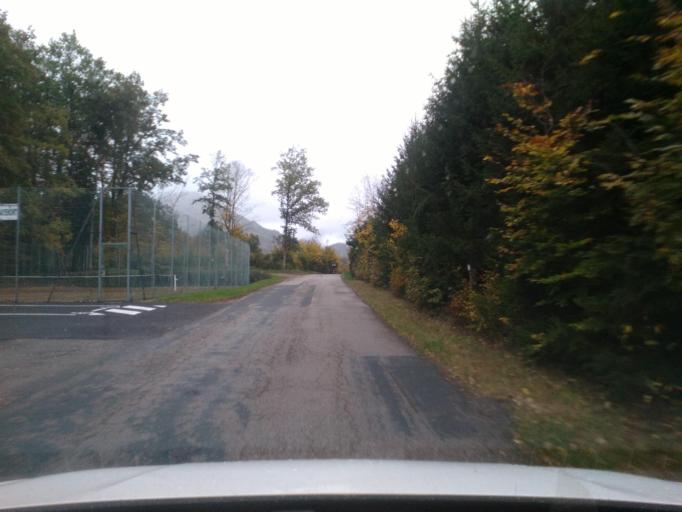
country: FR
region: Lorraine
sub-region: Departement des Vosges
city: Sainte-Marguerite
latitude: 48.2863
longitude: 7.0013
